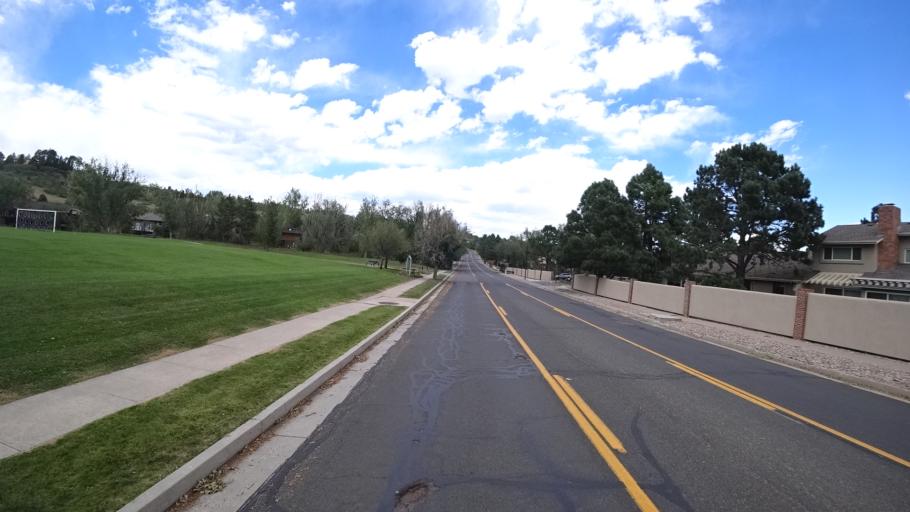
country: US
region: Colorado
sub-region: El Paso County
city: Stratmoor
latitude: 38.7787
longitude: -104.8316
